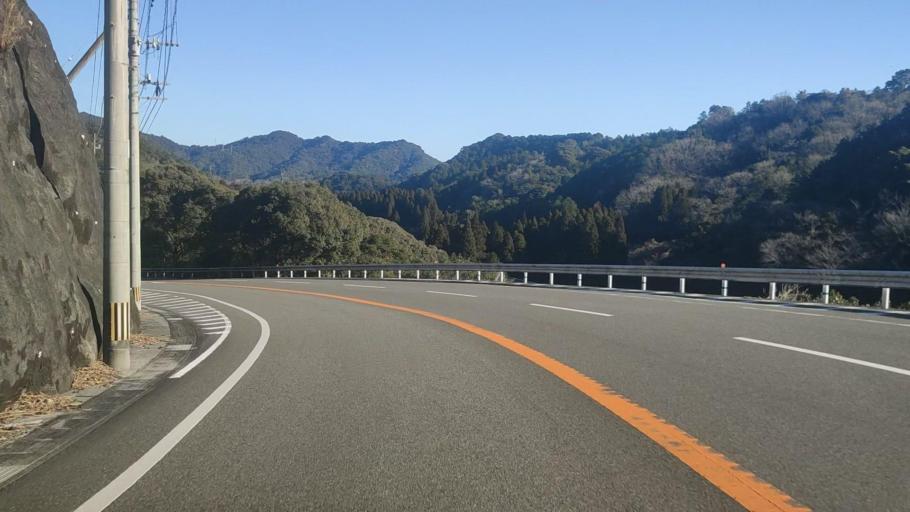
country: JP
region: Miyazaki
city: Nobeoka
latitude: 32.6348
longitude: 131.7406
